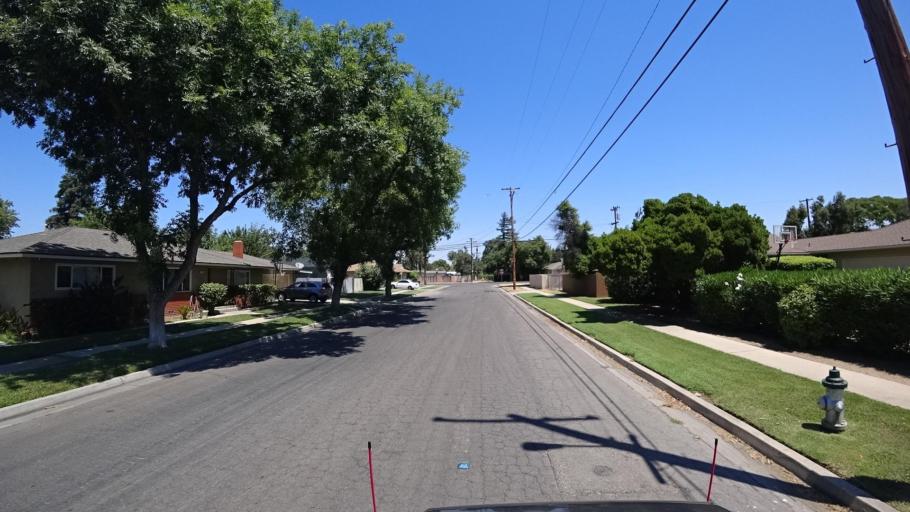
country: US
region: California
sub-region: Fresno County
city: Fresno
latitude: 36.7860
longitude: -119.7770
